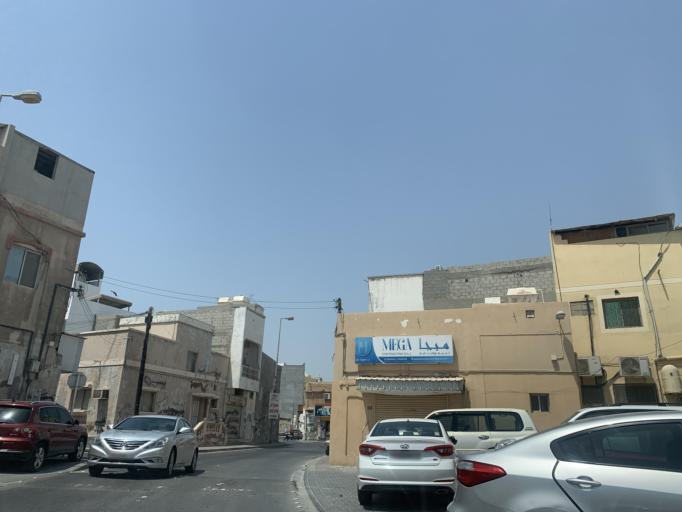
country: BH
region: Manama
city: Jidd Hafs
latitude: 26.2090
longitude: 50.5562
